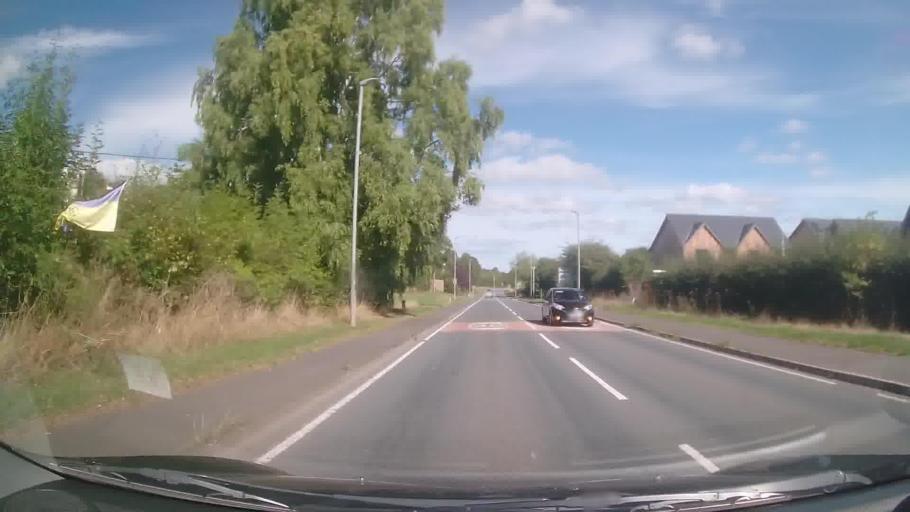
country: GB
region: Wales
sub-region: Sir Powys
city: Hay
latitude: 52.0864
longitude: -3.1491
